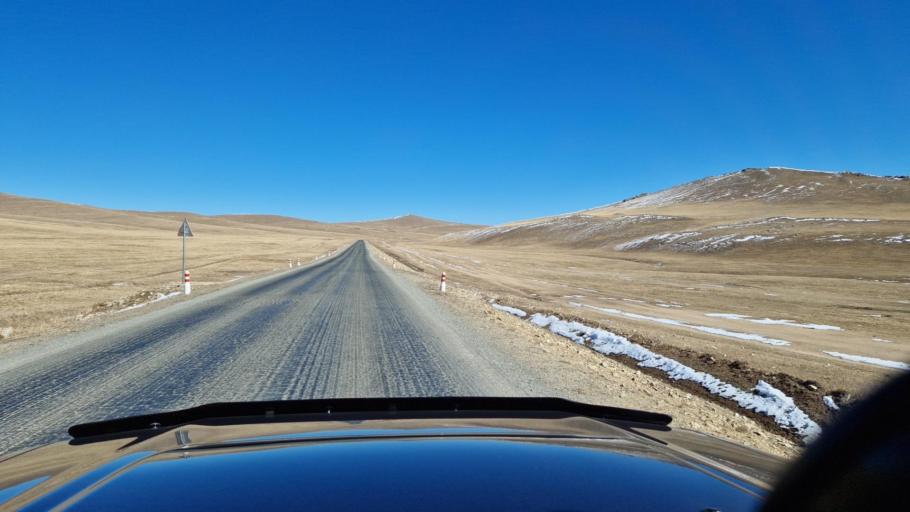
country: MN
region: Hentiy
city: Modot
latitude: 47.7978
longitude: 108.6946
